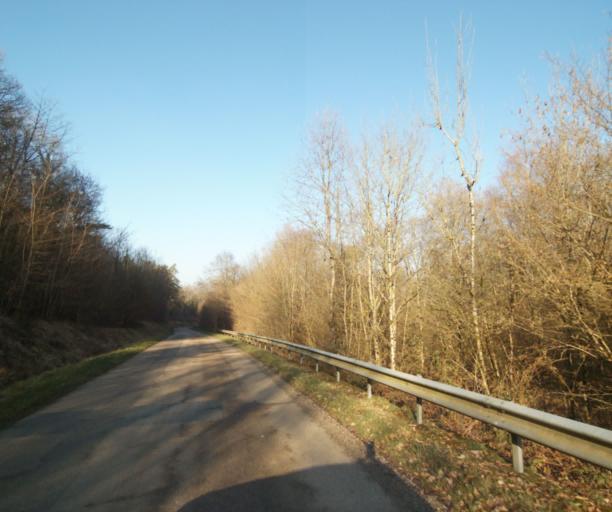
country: FR
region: Champagne-Ardenne
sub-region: Departement de la Haute-Marne
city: Chevillon
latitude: 48.5184
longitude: 5.0919
